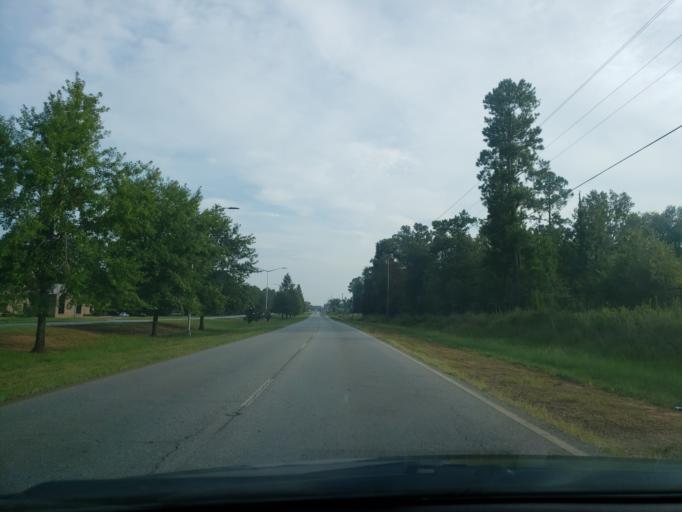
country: US
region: Georgia
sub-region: Dougherty County
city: Albany
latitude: 31.5791
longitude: -84.2193
